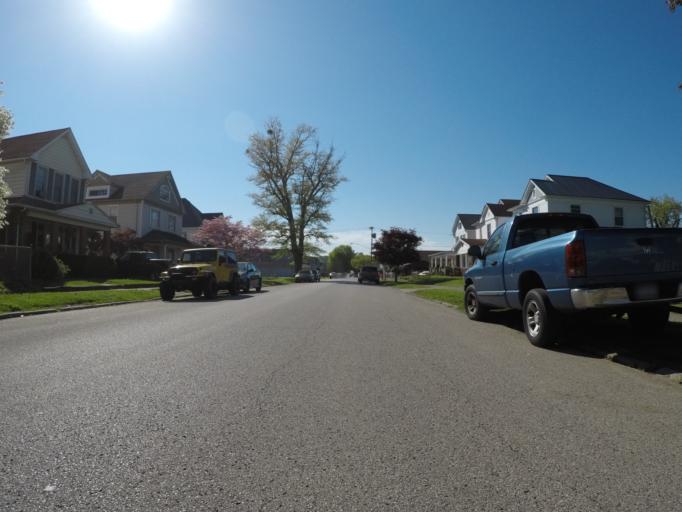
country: US
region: West Virginia
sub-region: Wayne County
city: Kenova
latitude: 38.4007
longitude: -82.5827
